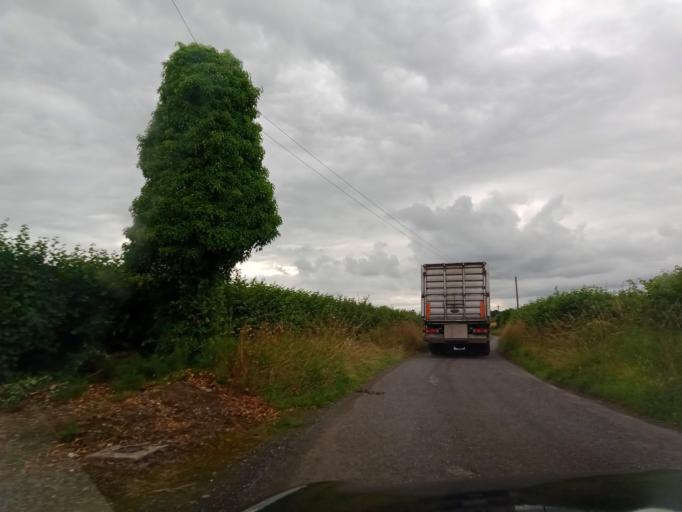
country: IE
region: Leinster
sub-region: Laois
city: Stradbally
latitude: 52.9611
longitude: -7.1710
